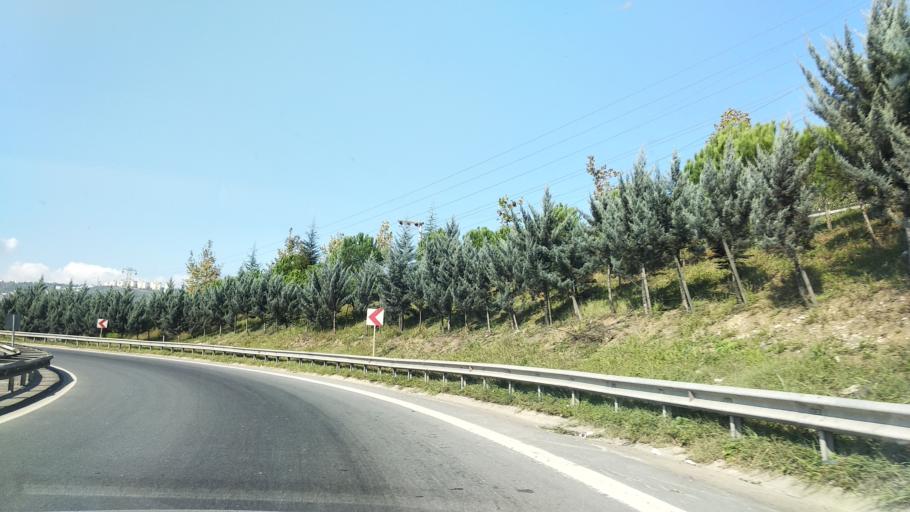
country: TR
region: Kocaeli
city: Kullar
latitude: 40.7827
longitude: 29.9782
